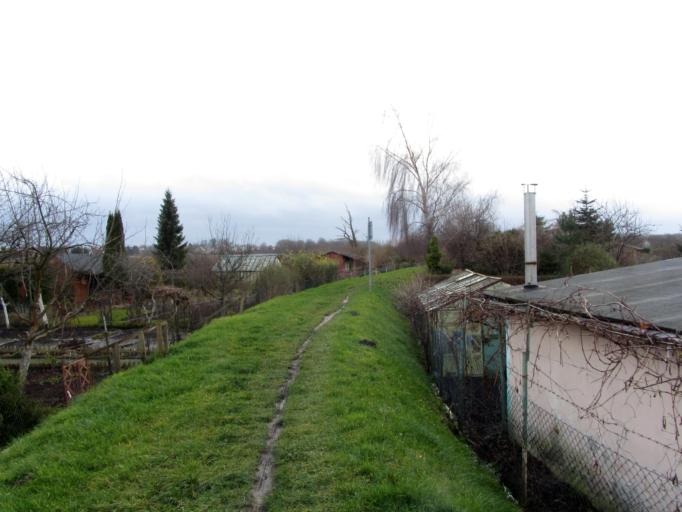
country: PL
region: West Pomeranian Voivodeship
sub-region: Powiat kolobrzeski
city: Kolobrzeg
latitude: 54.1686
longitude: 15.5785
